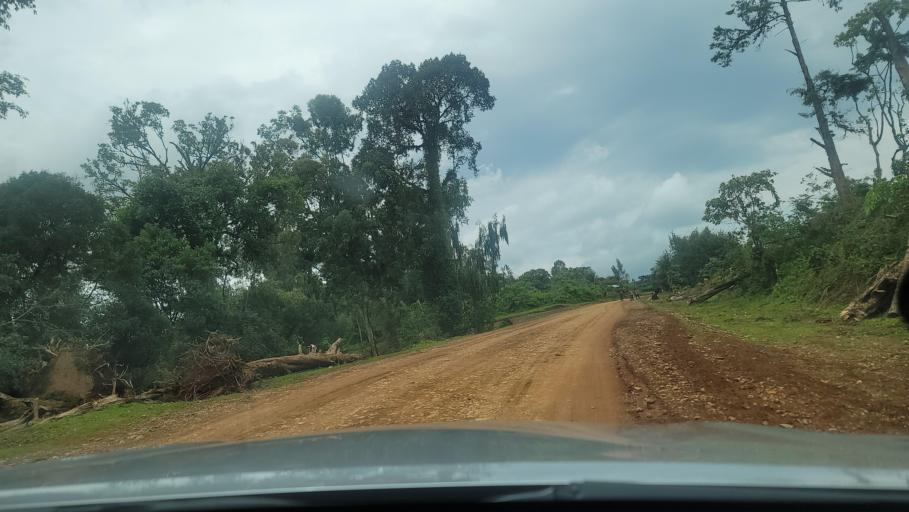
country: ET
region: Oromiya
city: Agaro
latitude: 7.7932
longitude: 36.4364
